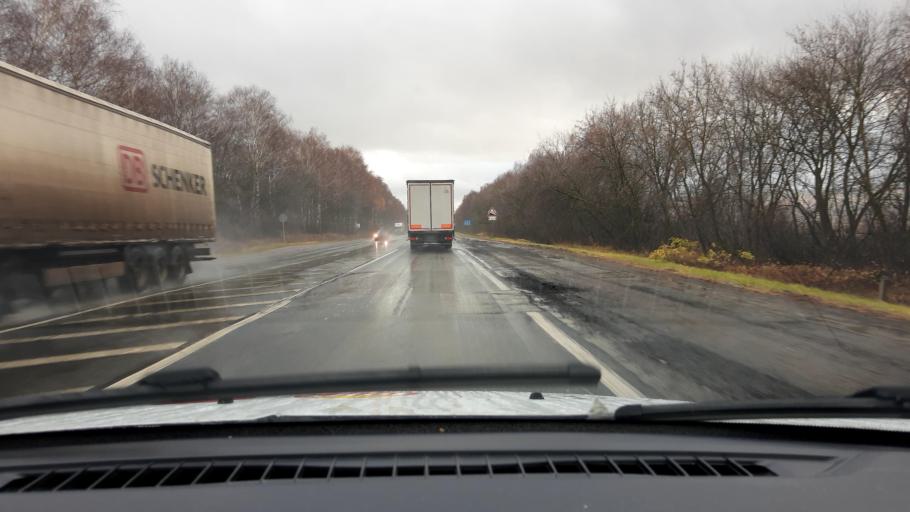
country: RU
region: Nizjnij Novgorod
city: Pamyat' Parizhskoy Kommuny
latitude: 56.0554
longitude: 44.4008
